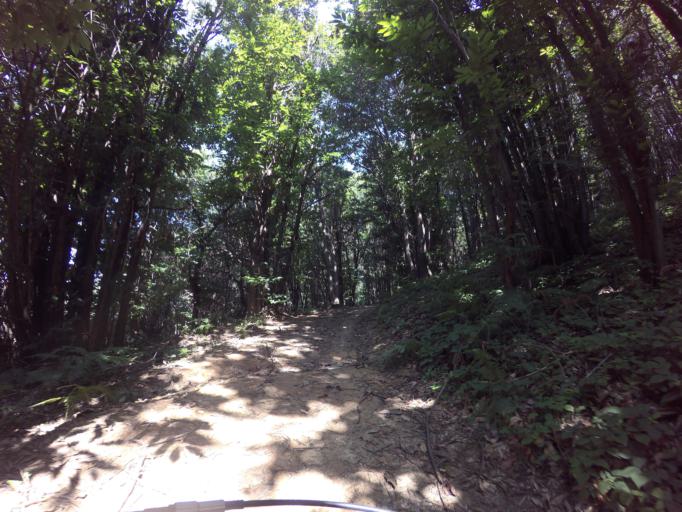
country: IT
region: Piedmont
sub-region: Provincia di Cuneo
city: Roccaforte Mondovi
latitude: 44.3282
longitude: 7.7125
